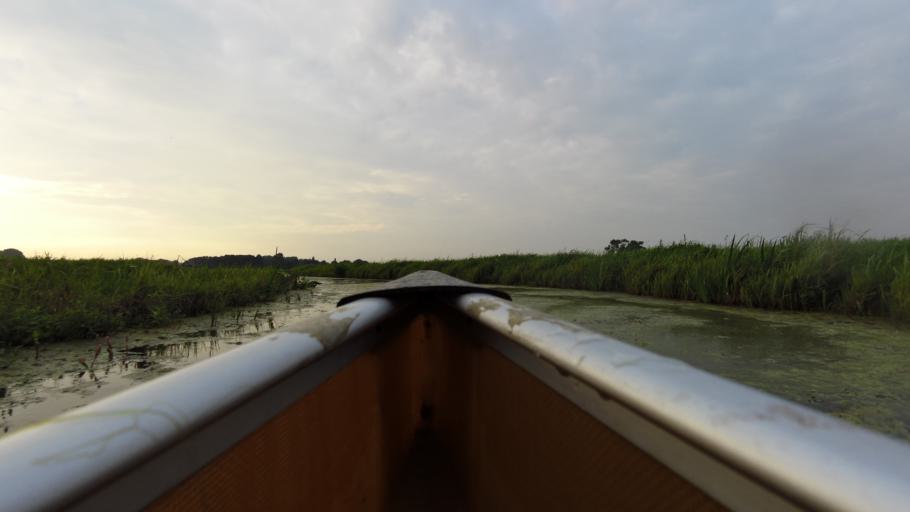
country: NL
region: South Holland
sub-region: Gemeente Leiderdorp
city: Leiderdorp
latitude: 52.1804
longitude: 4.5284
